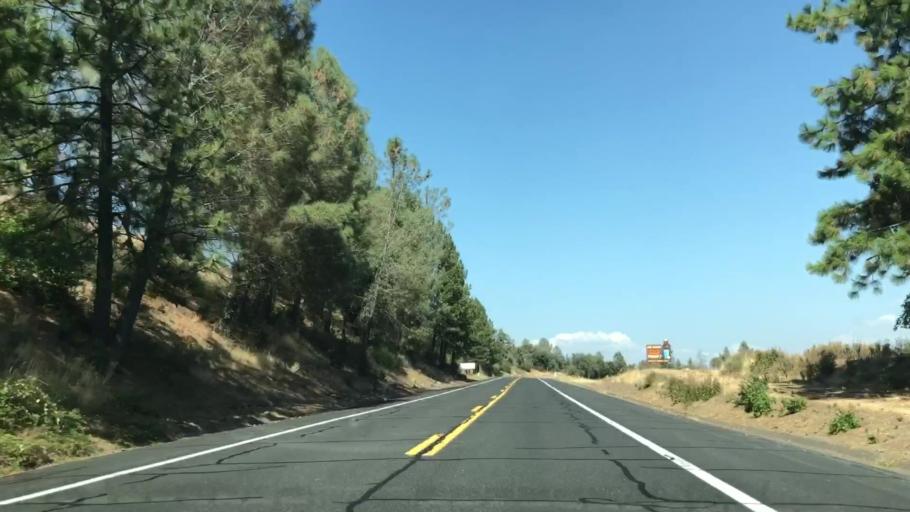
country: US
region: California
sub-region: Tuolumne County
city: Tuolumne City
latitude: 37.8224
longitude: -120.1013
